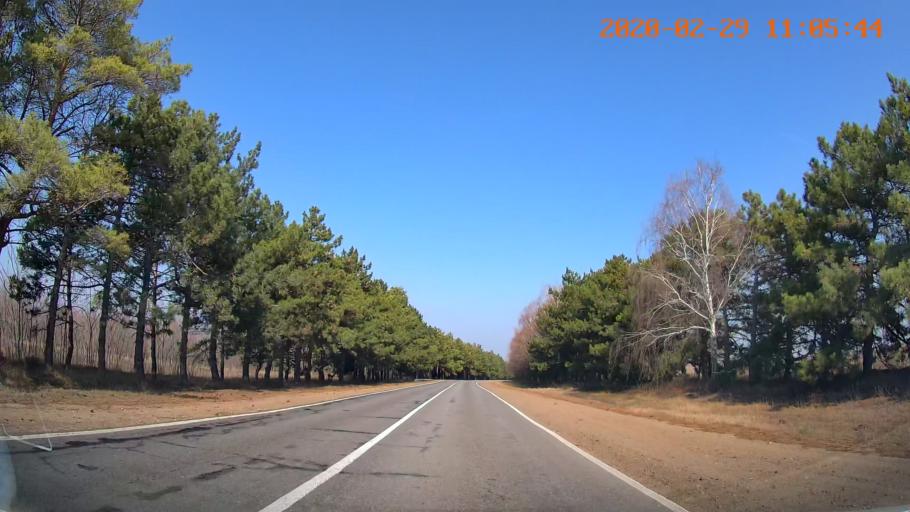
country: MD
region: Criuleni
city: Criuleni
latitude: 47.2058
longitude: 29.1905
